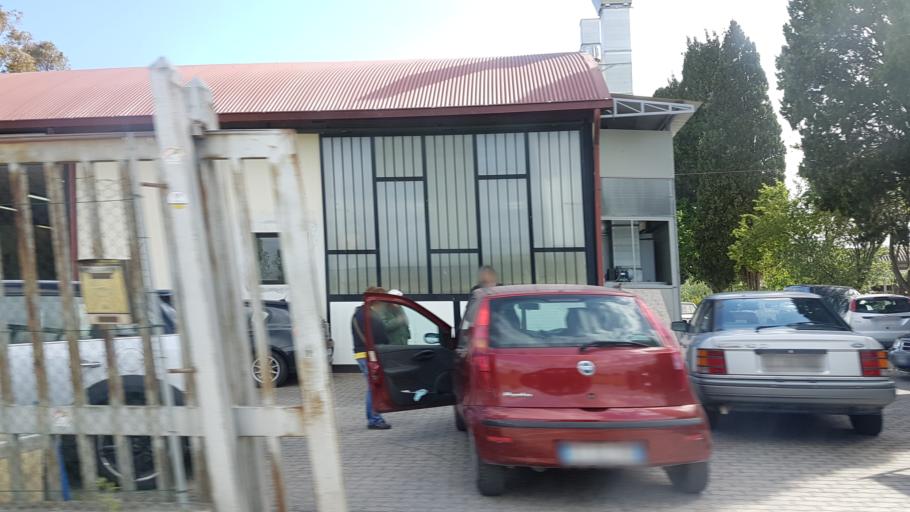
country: IT
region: Tuscany
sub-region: Provincia di Livorno
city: Rosignano Marittimo
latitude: 43.4385
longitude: 10.4854
